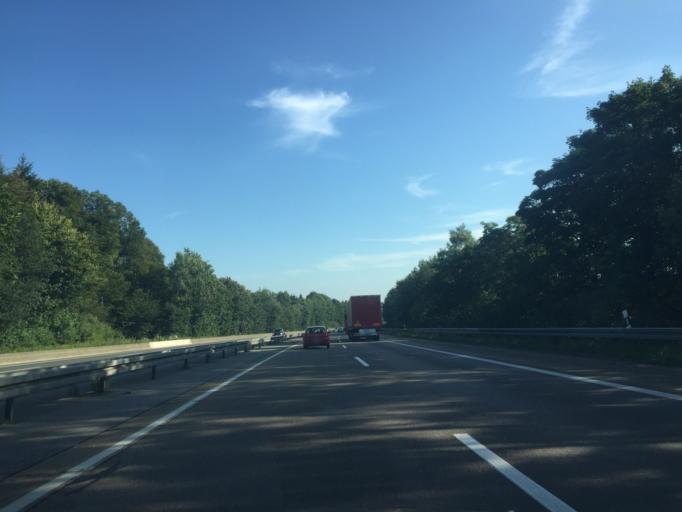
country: DE
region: North Rhine-Westphalia
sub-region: Regierungsbezirk Arnsberg
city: Luedenscheid
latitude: 51.1789
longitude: 7.6502
